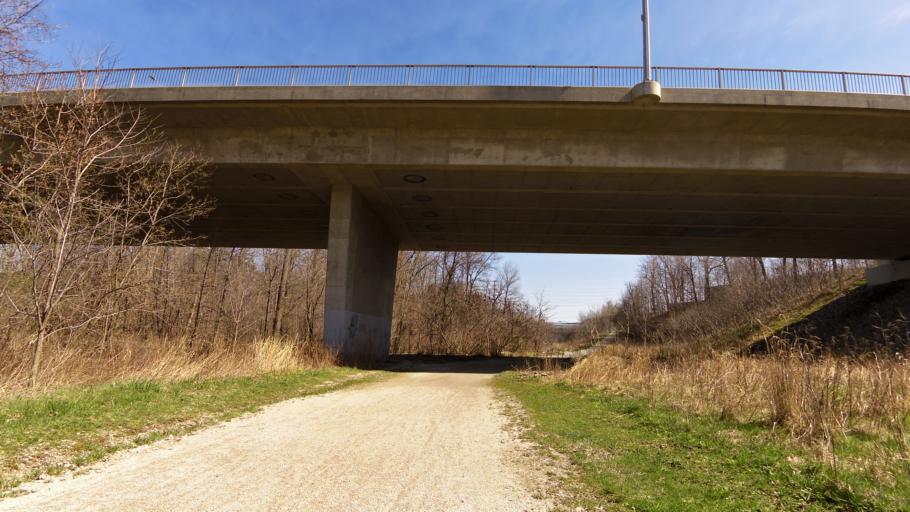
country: CA
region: Ontario
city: Etobicoke
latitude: 43.6515
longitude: -79.6180
